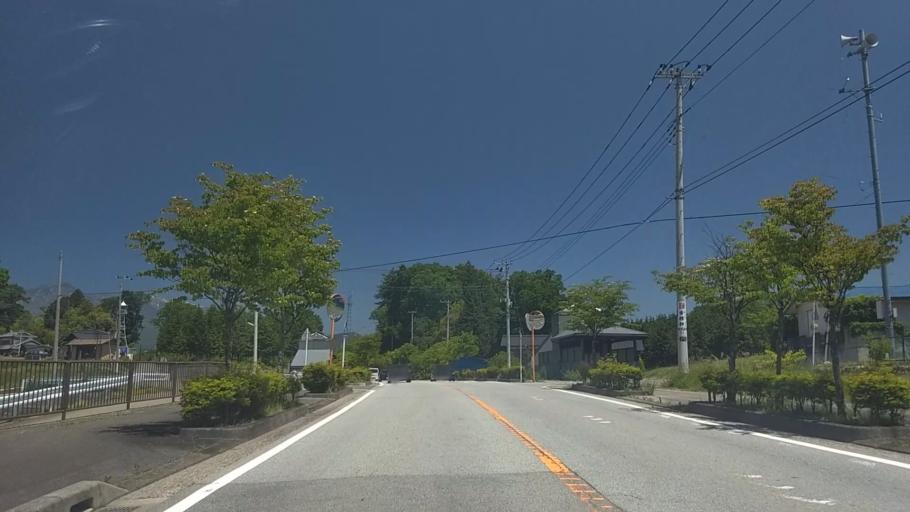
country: JP
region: Yamanashi
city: Nirasaki
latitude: 35.8172
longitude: 138.4293
